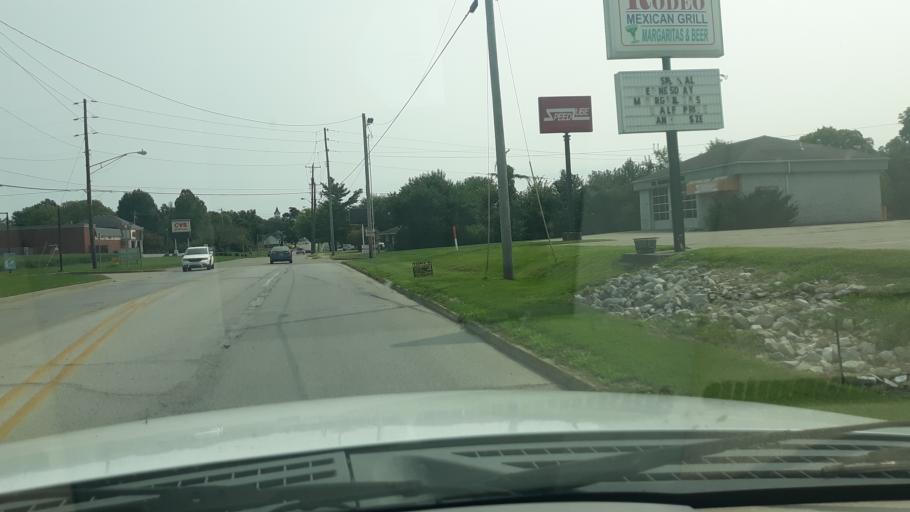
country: US
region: Indiana
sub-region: Gibson County
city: Princeton
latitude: 38.3554
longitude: -87.5806
